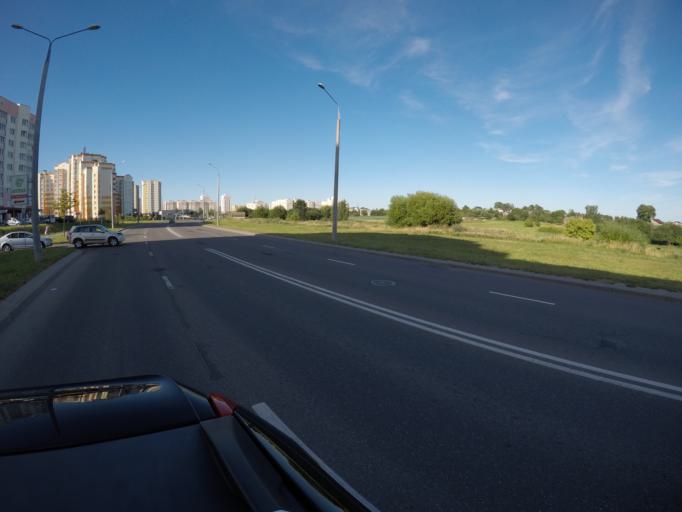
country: BY
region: Grodnenskaya
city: Hrodna
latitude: 53.7059
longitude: 23.8589
